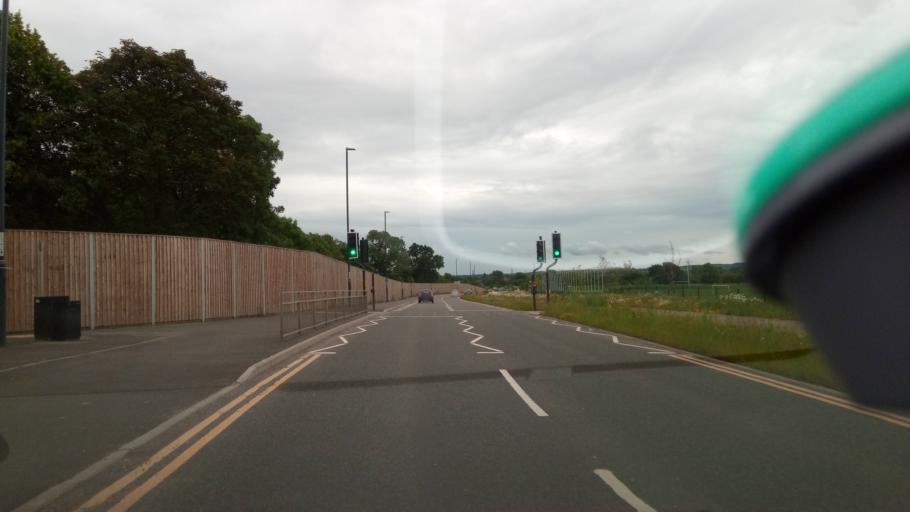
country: GB
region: England
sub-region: Derby
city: Derby
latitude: 52.8879
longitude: -1.4575
